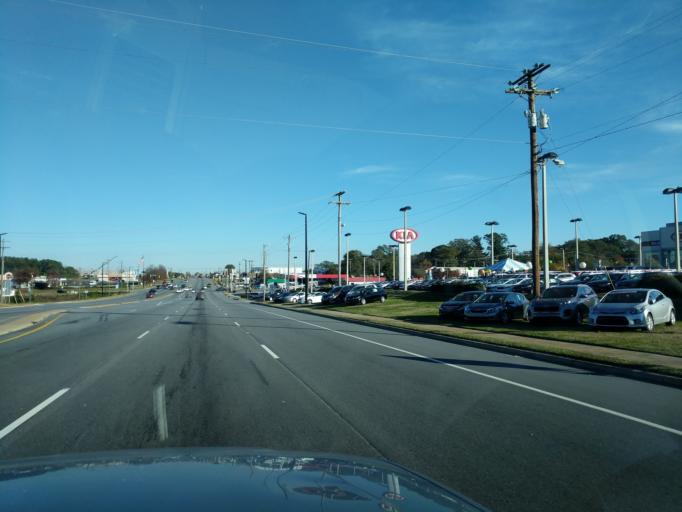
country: US
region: South Carolina
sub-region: Greenville County
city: Greer
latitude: 34.9479
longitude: -82.2192
